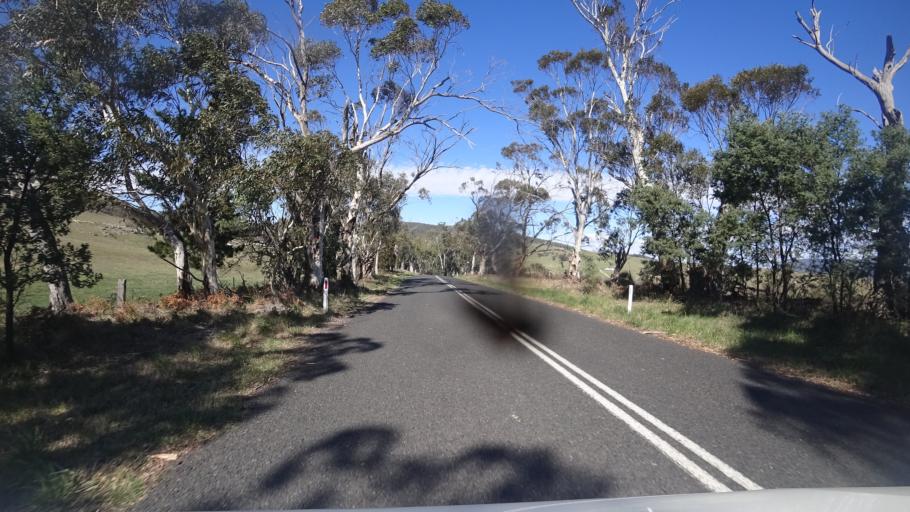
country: AU
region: New South Wales
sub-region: Lithgow
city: Bowenfels
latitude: -33.5182
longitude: 149.9879
